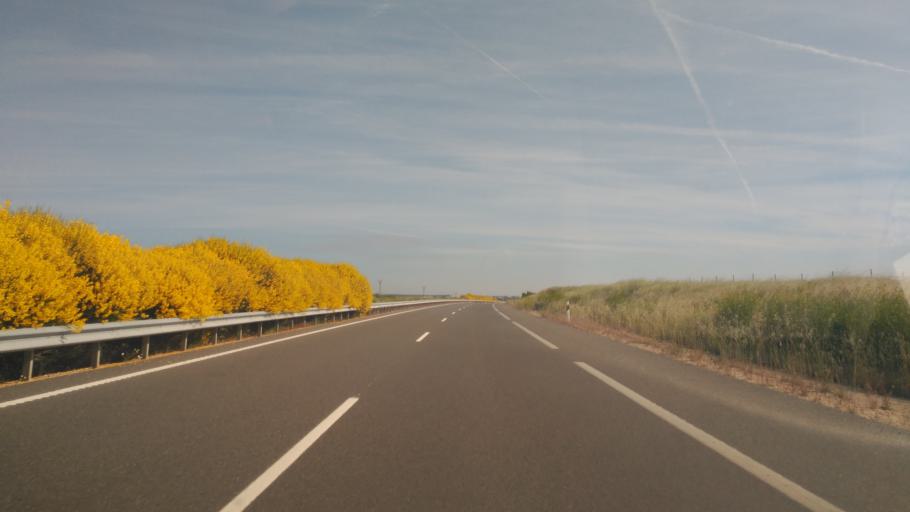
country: ES
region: Castille and Leon
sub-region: Provincia de Salamanca
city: Calzada de Valdunciel
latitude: 41.1047
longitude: -5.6986
